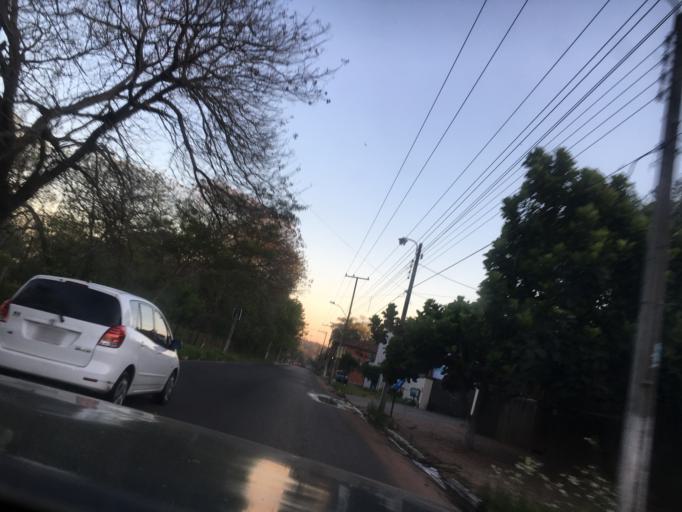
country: PY
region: Central
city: Lambare
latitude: -25.3454
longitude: -57.6020
